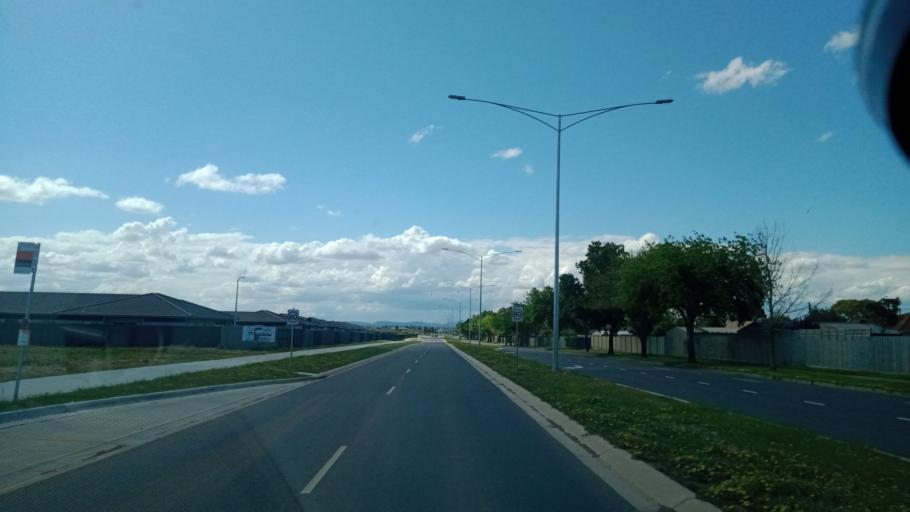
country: AU
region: Victoria
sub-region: Casey
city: Cranbourne West
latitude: -38.1071
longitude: 145.2527
